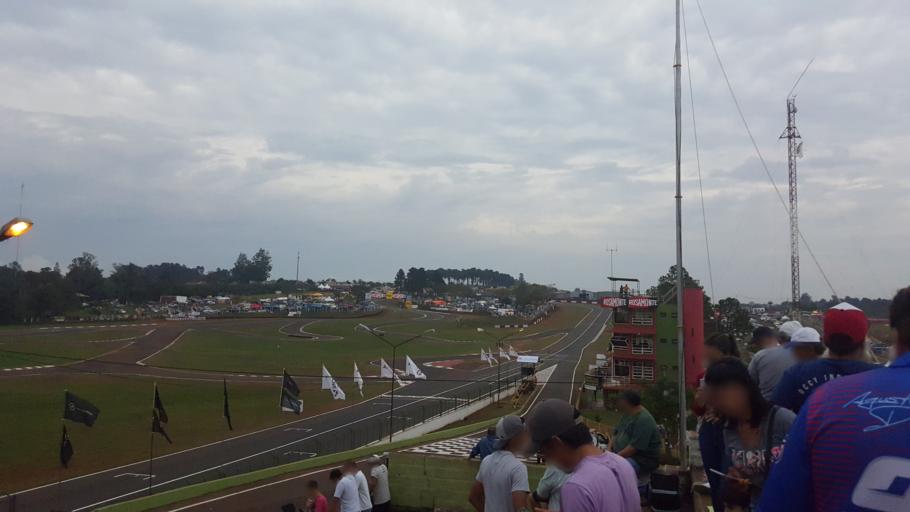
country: AR
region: Entre Rios
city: Concepcion del Uruguay
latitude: -32.4549
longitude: -58.3183
